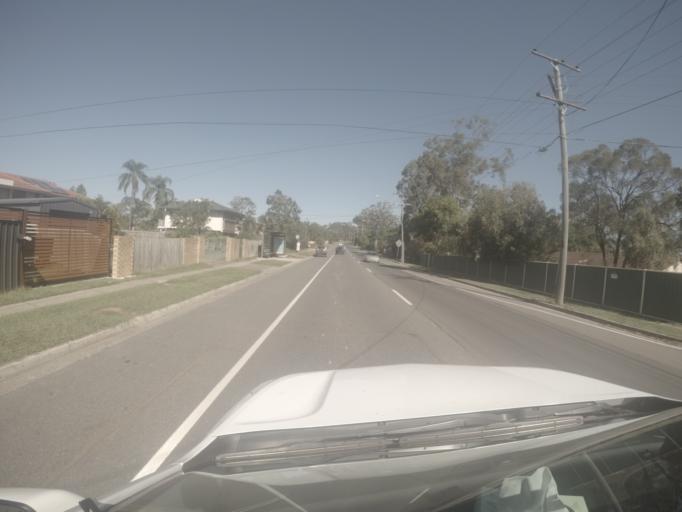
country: AU
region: Queensland
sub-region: Ipswich
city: Goodna
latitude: -27.6243
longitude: 152.9149
